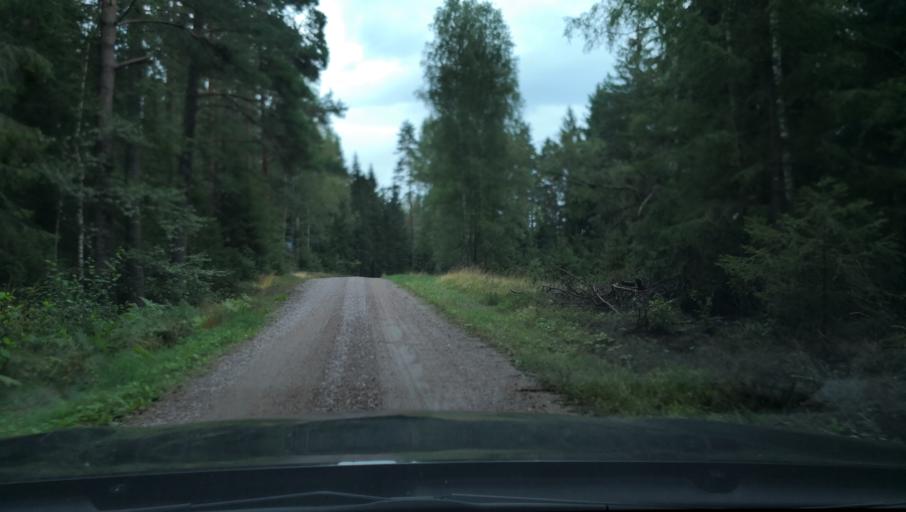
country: SE
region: Vaestmanland
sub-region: Arboga Kommun
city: Tyringe
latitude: 59.3562
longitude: 15.9981
